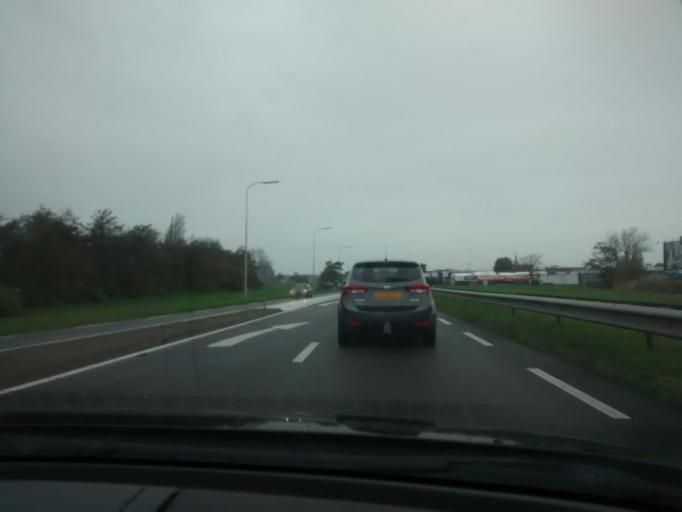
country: NL
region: South Holland
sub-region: Gemeente Katwijk
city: Rijnsburg
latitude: 52.1722
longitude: 4.4400
